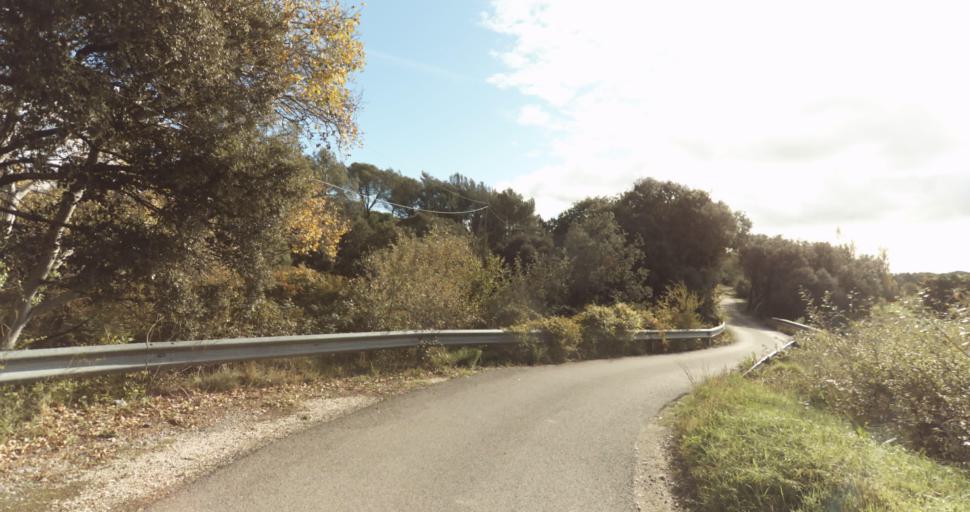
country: FR
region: Provence-Alpes-Cote d'Azur
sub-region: Departement des Bouches-du-Rhone
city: Venelles
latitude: 43.5860
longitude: 5.5000
